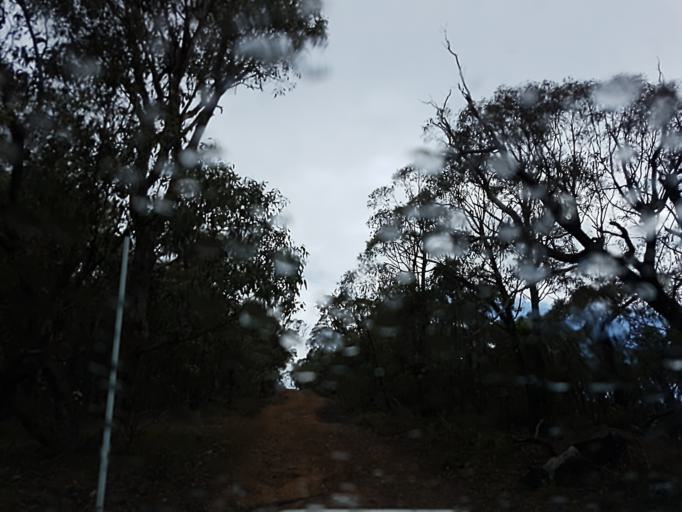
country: AU
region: New South Wales
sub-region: Snowy River
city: Jindabyne
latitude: -36.9072
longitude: 148.3402
